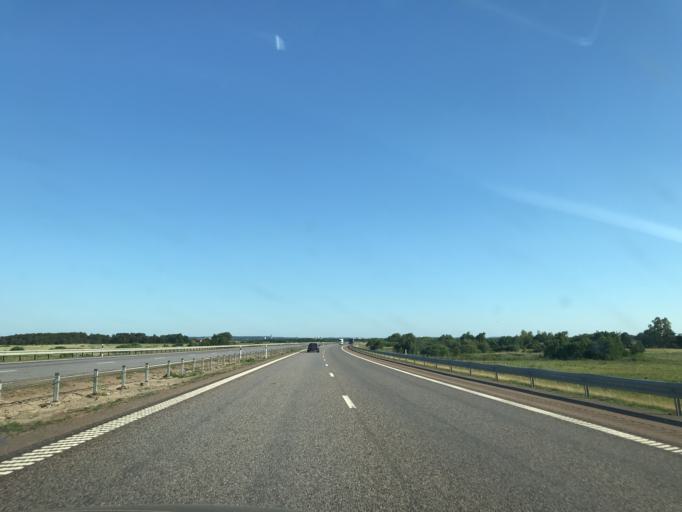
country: SE
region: Halland
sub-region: Halmstads Kommun
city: Troenninge
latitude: 56.6090
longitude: 12.9193
